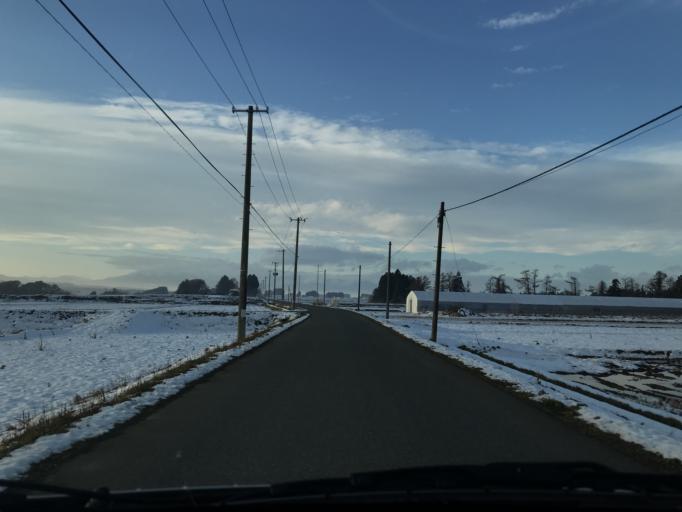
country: JP
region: Iwate
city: Mizusawa
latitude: 39.0471
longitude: 141.1072
